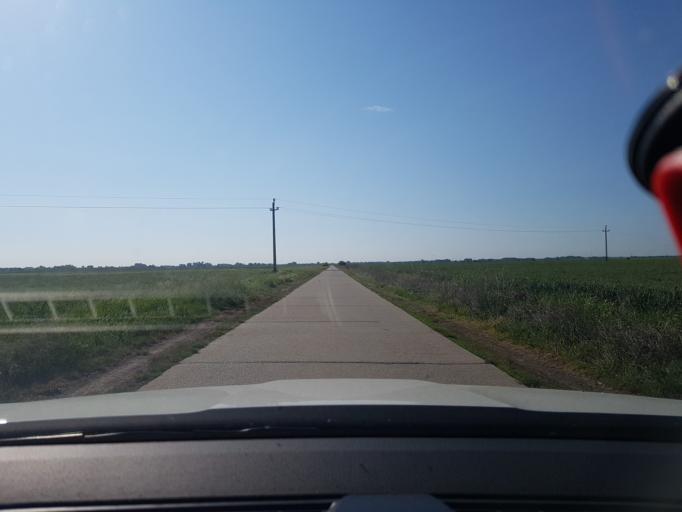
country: HU
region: Tolna
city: Decs
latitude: 46.2829
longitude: 18.6991
